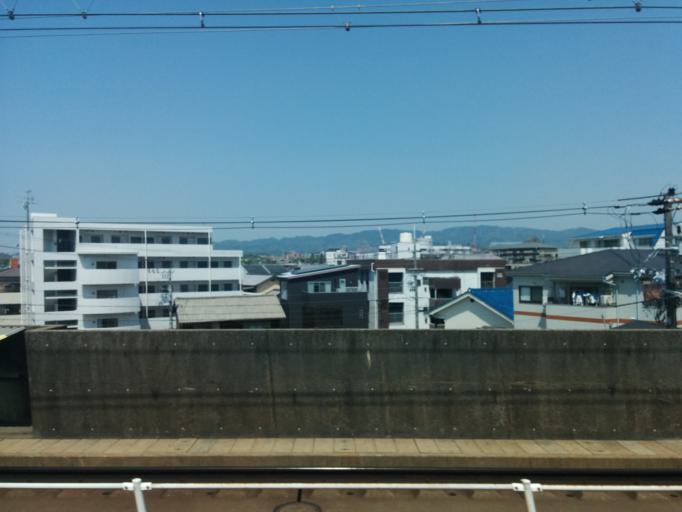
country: JP
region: Osaka
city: Ibaraki
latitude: 34.8193
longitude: 135.5781
